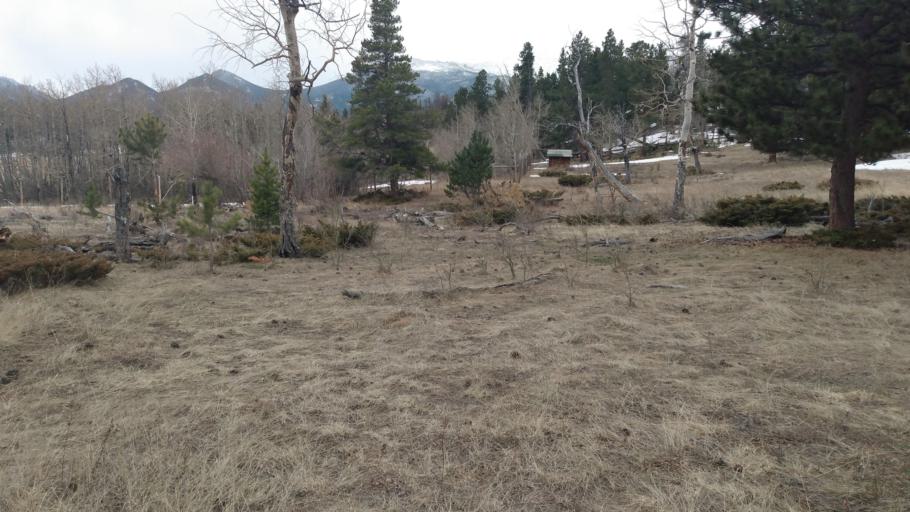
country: US
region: Colorado
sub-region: Larimer County
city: Estes Park
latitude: 40.3732
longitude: -105.6157
